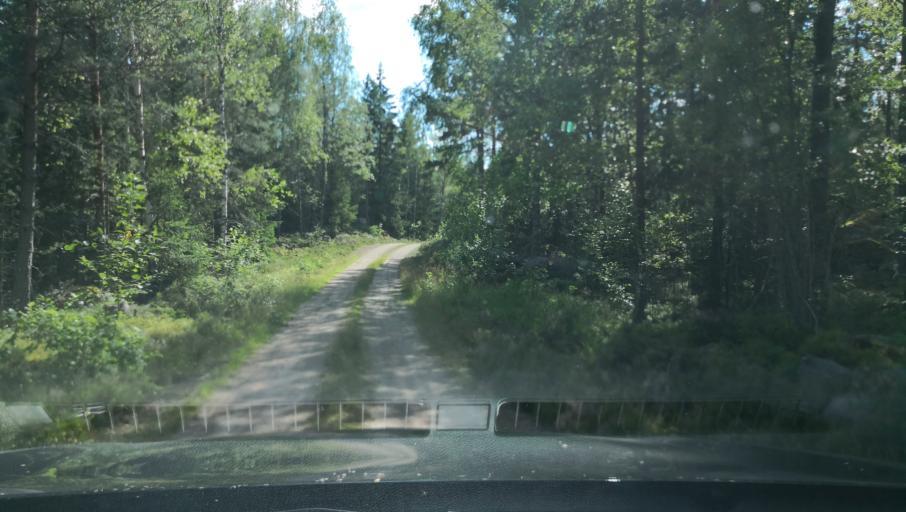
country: SE
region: Vaestmanland
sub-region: Vasteras
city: Skultuna
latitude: 59.7132
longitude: 16.3715
